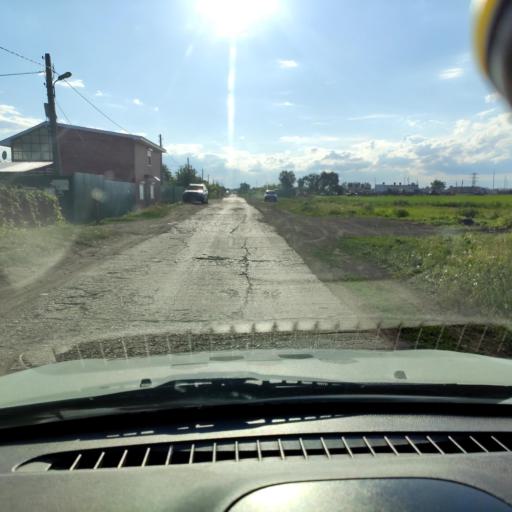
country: RU
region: Samara
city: Tol'yatti
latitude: 53.5905
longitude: 49.4459
